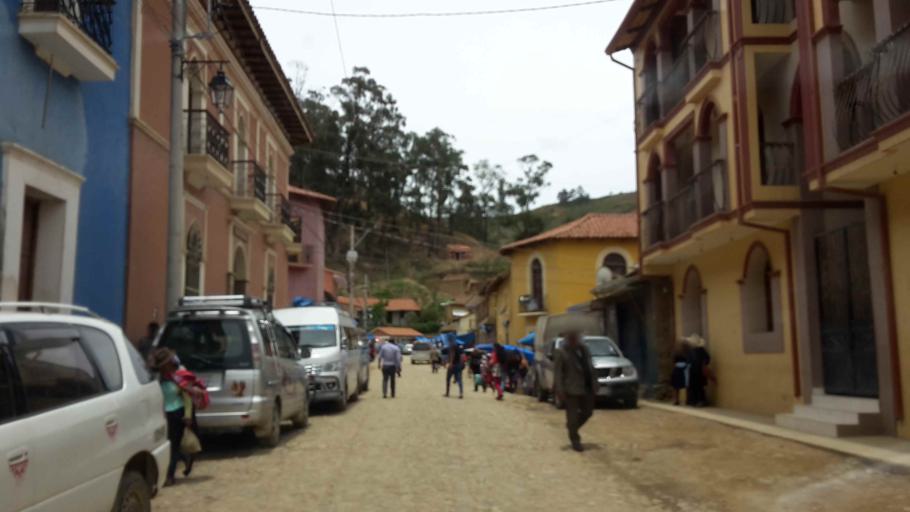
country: BO
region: Cochabamba
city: Totora
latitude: -17.7354
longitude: -65.1919
